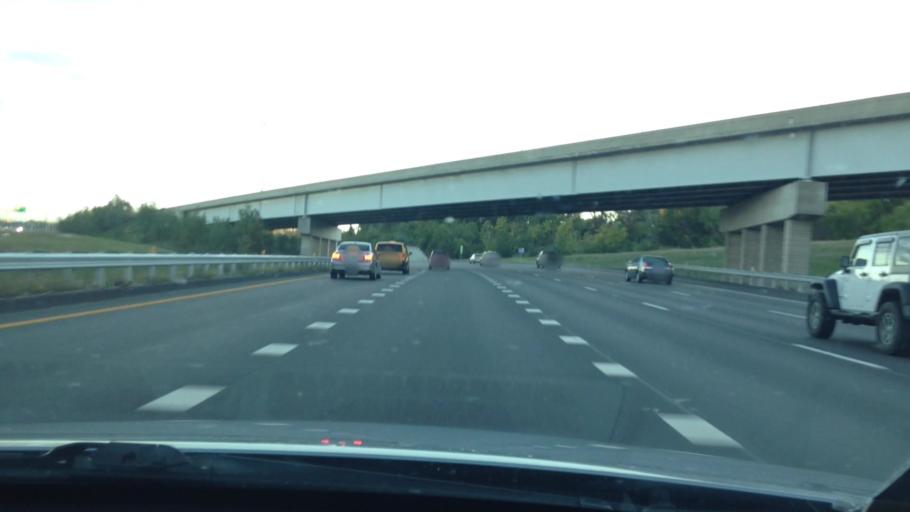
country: US
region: Missouri
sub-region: Jackson County
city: Raytown
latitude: 39.0213
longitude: -94.5011
